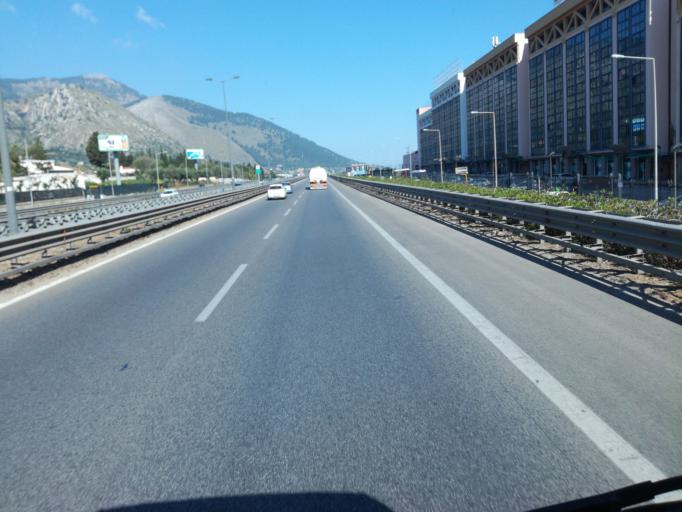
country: IT
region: Sicily
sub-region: Palermo
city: Palermo
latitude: 38.1619
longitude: 13.3104
